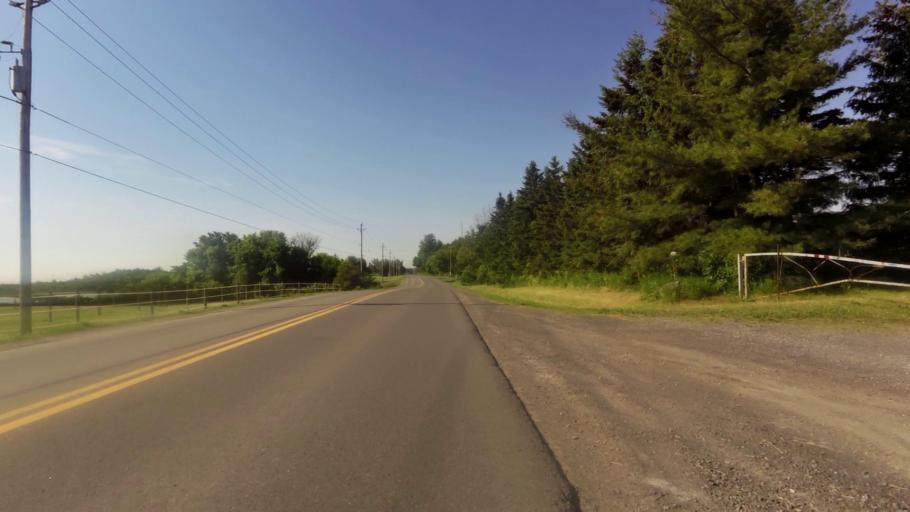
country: CA
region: Ontario
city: Ottawa
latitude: 45.2376
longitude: -75.5611
